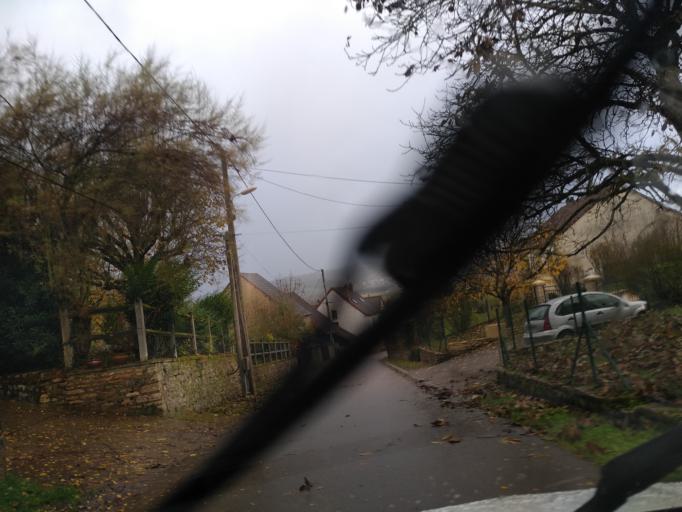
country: FR
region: Bourgogne
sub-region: Departement de Saone-et-Loire
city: Saint-Leger-sur-Dheune
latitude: 46.8763
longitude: 4.6663
